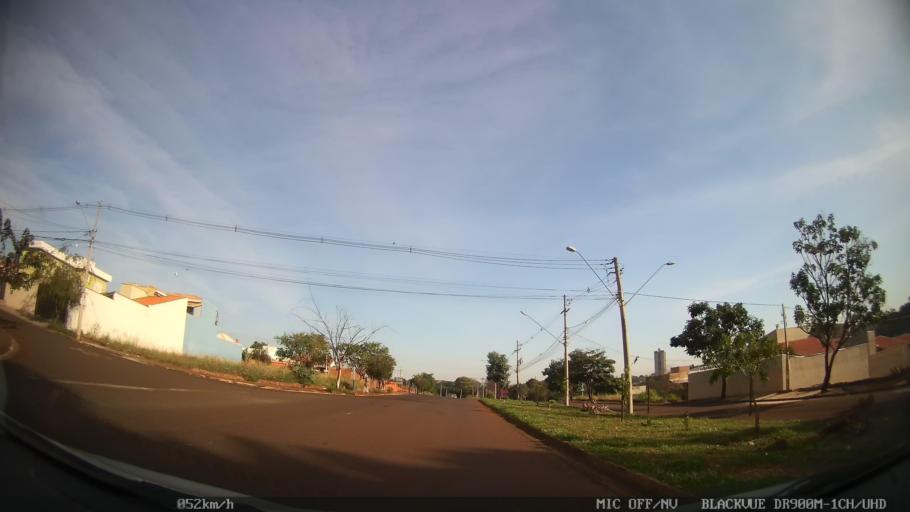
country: BR
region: Sao Paulo
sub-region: Ribeirao Preto
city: Ribeirao Preto
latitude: -21.2767
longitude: -47.8065
